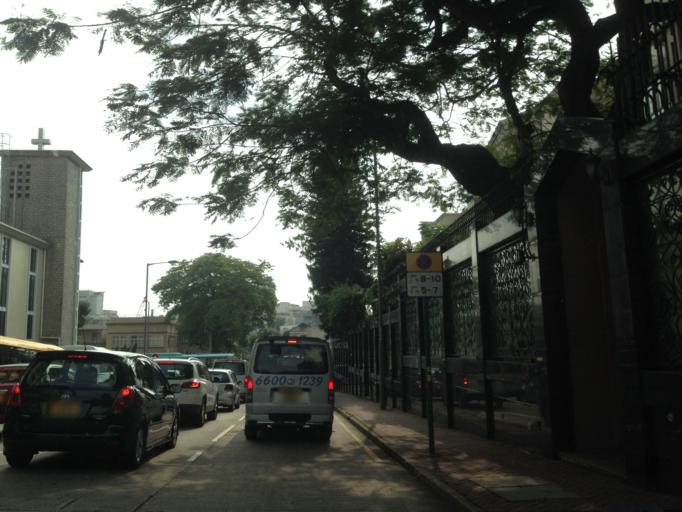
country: HK
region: Kowloon City
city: Kowloon
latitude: 22.3303
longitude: 114.1795
